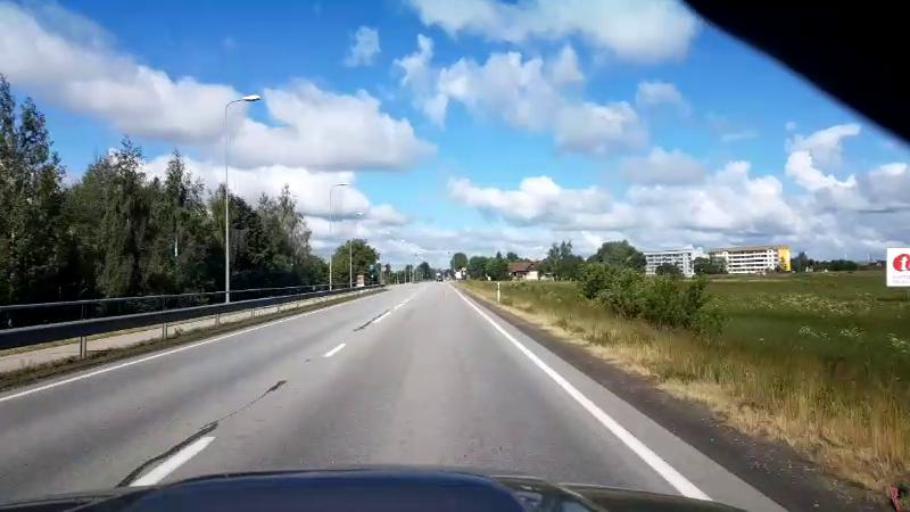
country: LV
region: Bauskas Rajons
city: Bauska
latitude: 56.4043
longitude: 24.2107
